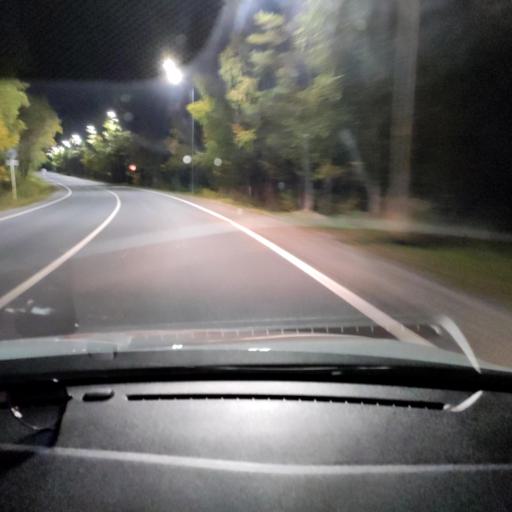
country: RU
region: Tatarstan
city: Verkhniy Uslon
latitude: 55.6365
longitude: 49.0218
